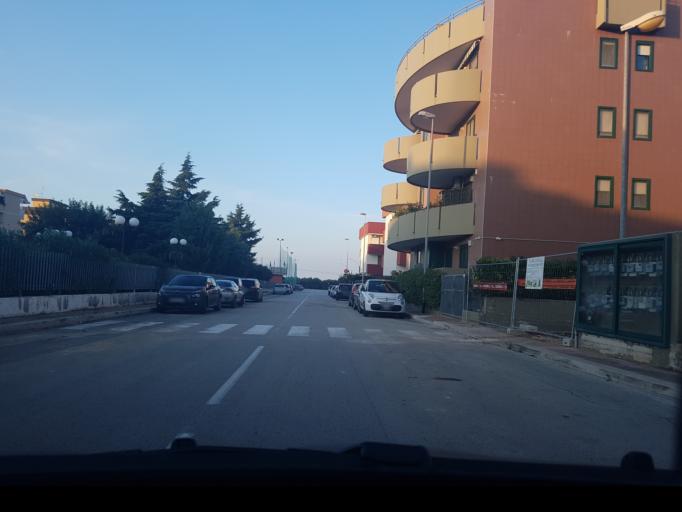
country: IT
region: Apulia
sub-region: Provincia di Bari
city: Bitritto
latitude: 41.0483
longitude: 16.8252
